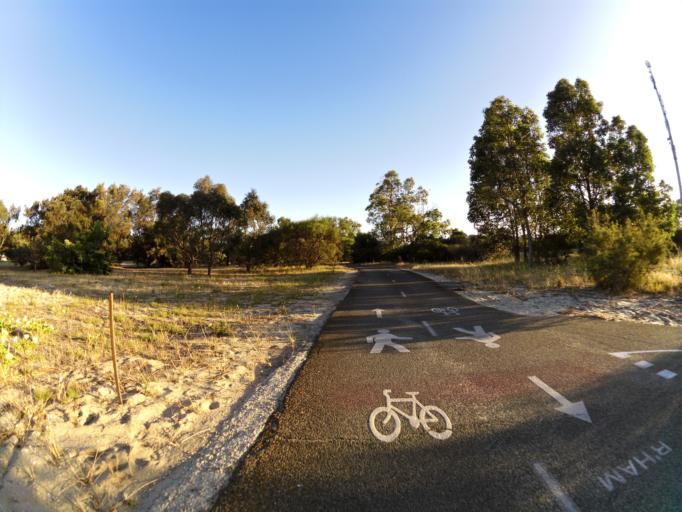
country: AU
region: Western Australia
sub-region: South Perth
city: Manning
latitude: -32.0094
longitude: 115.8548
